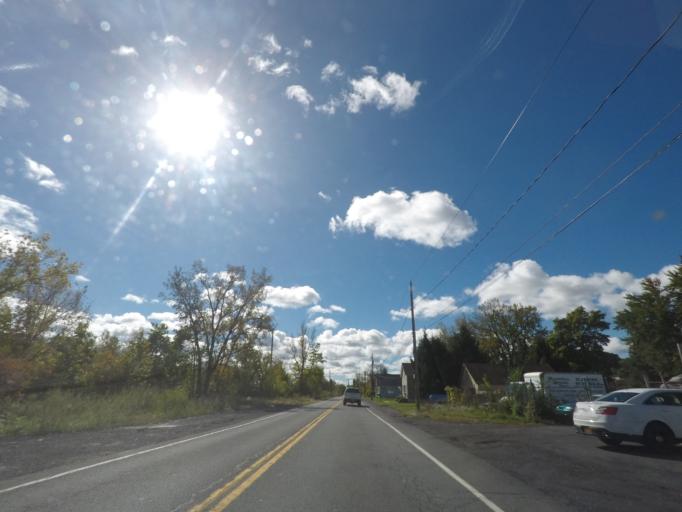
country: US
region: New York
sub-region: Albany County
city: Watervliet
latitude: 42.7157
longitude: -73.7183
